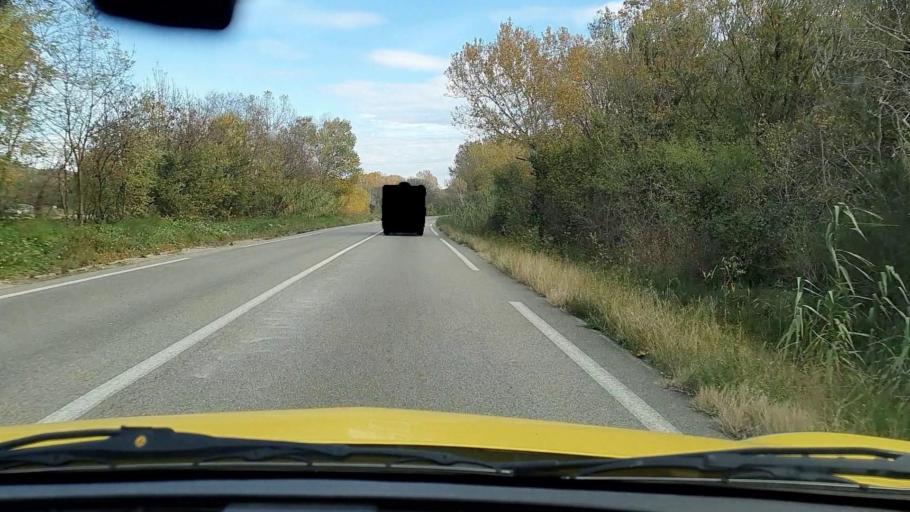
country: FR
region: Languedoc-Roussillon
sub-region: Departement du Gard
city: Aramon
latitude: 43.9029
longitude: 4.7035
